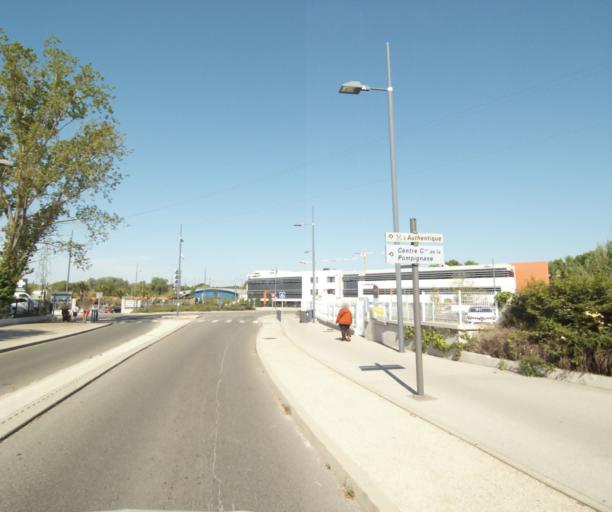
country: FR
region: Languedoc-Roussillon
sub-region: Departement de l'Herault
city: Castelnau-le-Lez
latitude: 43.6263
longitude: 3.9018
